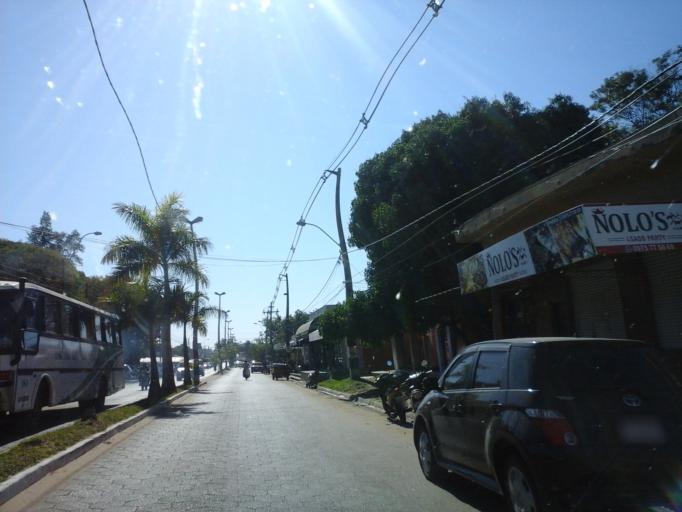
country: PY
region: Neembucu
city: Pilar
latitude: -26.8690
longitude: -58.3023
